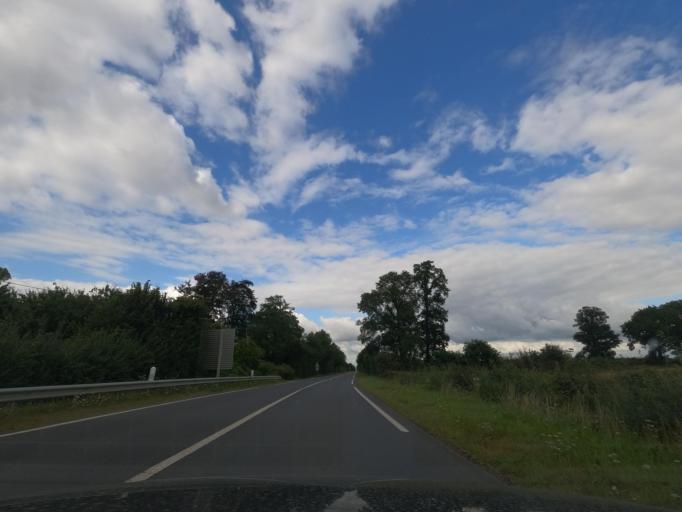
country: FR
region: Lower Normandy
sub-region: Departement du Calvados
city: Orbec
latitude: 48.8937
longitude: 0.4015
